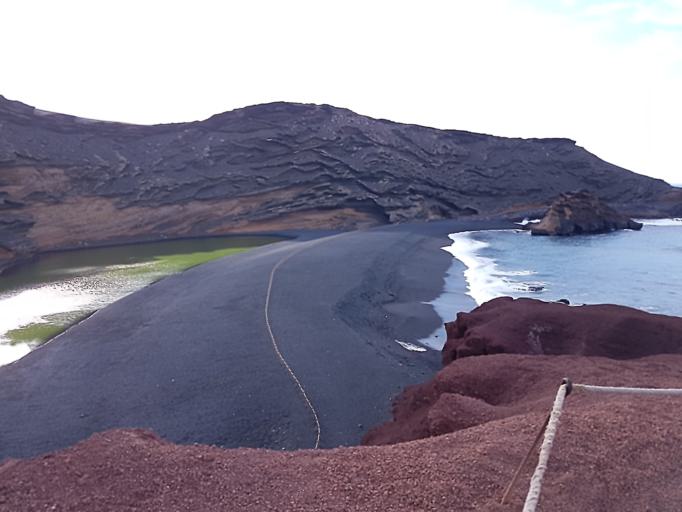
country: ES
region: Canary Islands
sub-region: Provincia de Las Palmas
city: Yaiza
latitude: 28.9781
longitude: -13.8287
